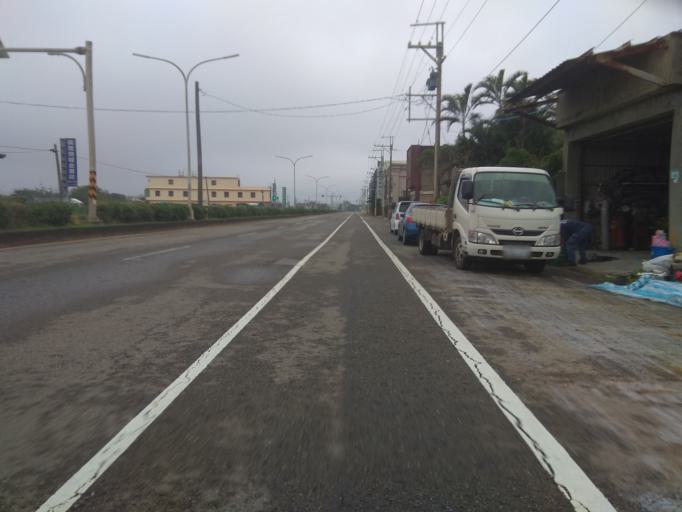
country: TW
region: Taiwan
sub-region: Hsinchu
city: Zhubei
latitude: 25.0280
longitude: 121.0786
